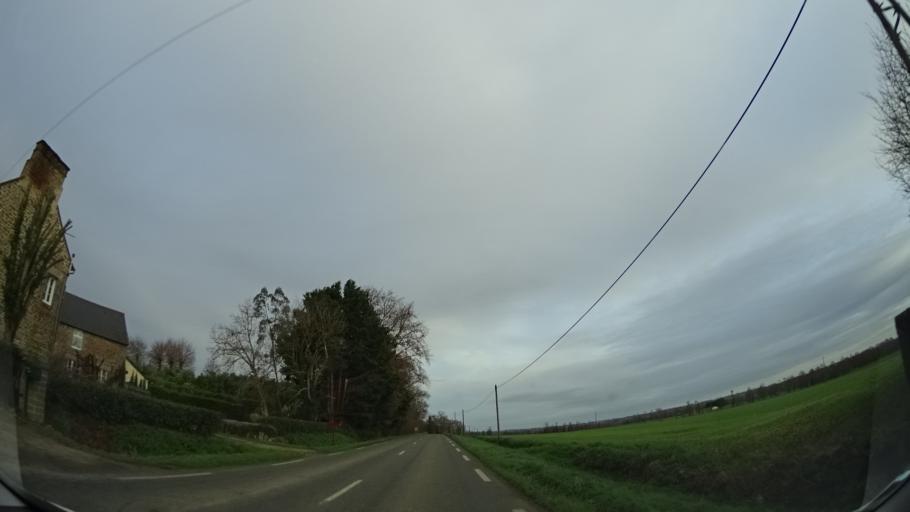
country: FR
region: Brittany
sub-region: Departement des Cotes-d'Armor
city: Evran
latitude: 48.3640
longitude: -1.9704
